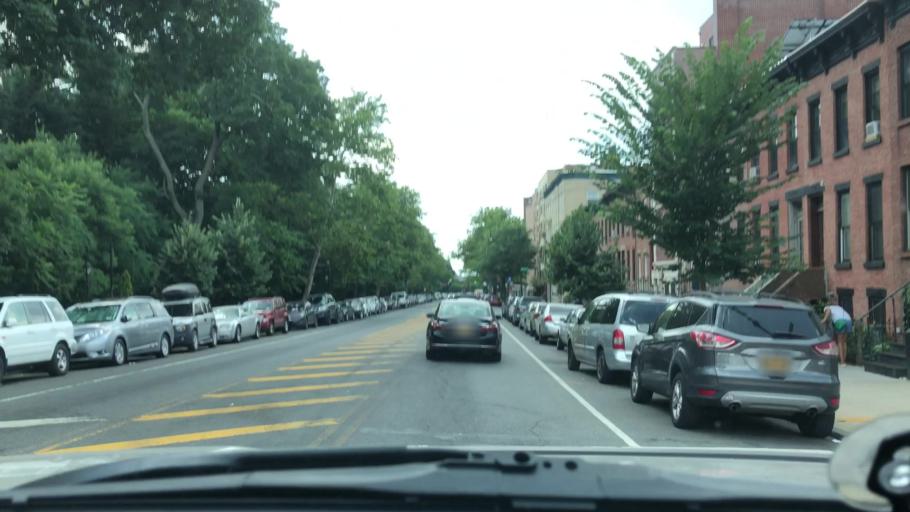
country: US
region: New York
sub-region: Kings County
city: Brooklyn
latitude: 40.6546
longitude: -73.9733
